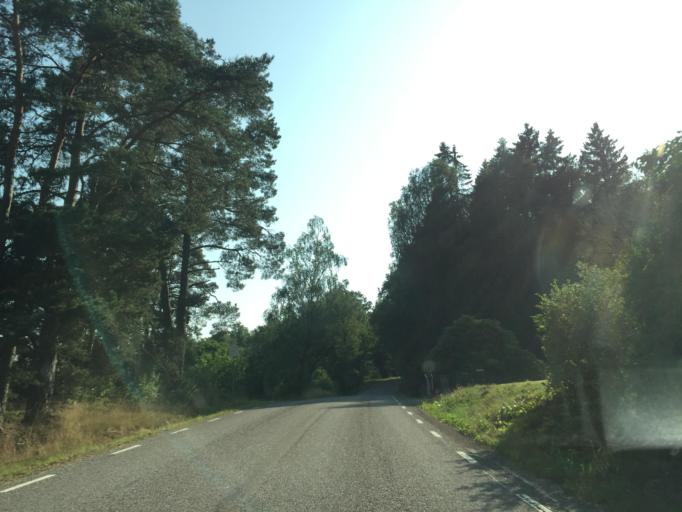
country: SE
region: Vaestra Goetaland
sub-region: Trollhattan
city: Sjuntorp
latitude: 58.2491
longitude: 12.2036
